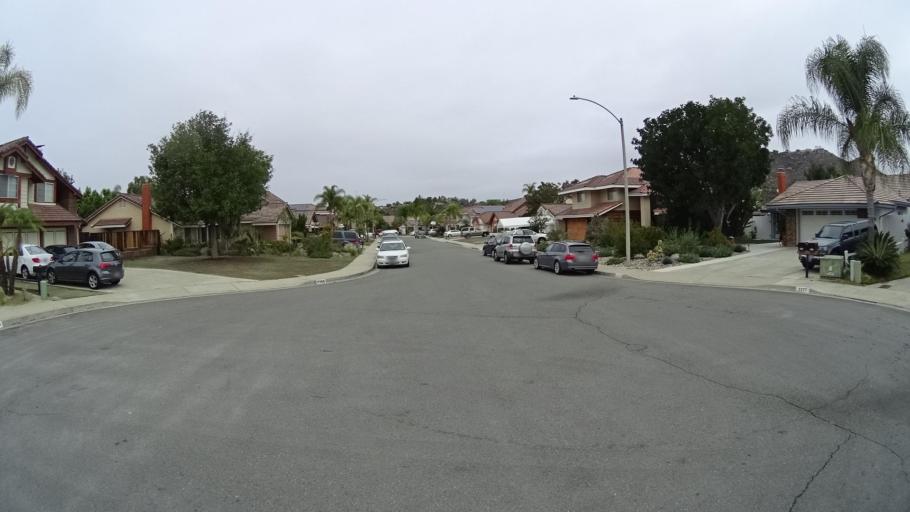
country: US
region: California
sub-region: San Diego County
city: Rancho San Diego
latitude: 32.7577
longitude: -116.9065
